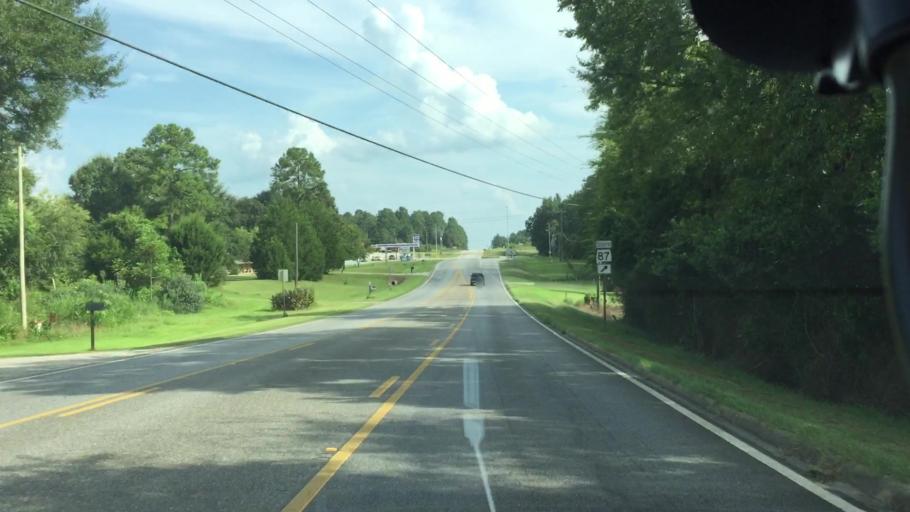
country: US
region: Alabama
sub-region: Pike County
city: Troy
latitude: 31.6820
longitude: -85.9585
